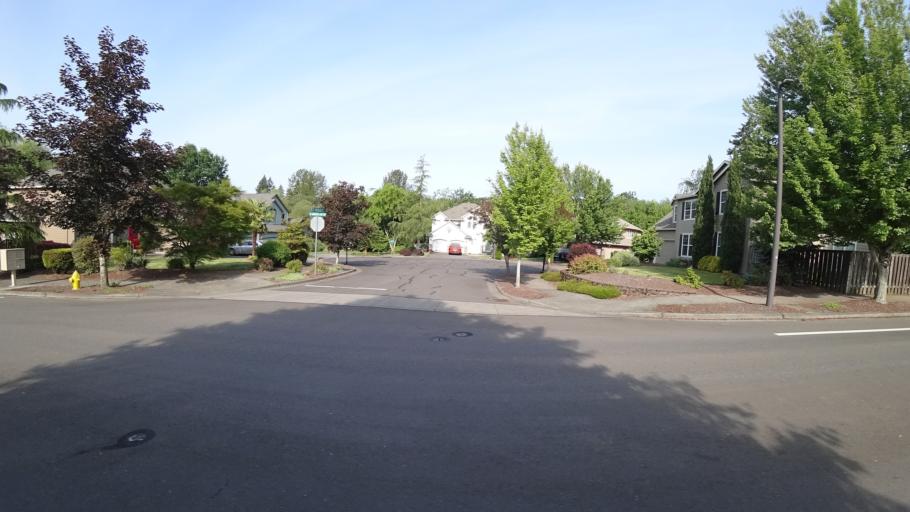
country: US
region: Oregon
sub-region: Clackamas County
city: Happy Valley
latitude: 45.4460
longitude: -122.5247
